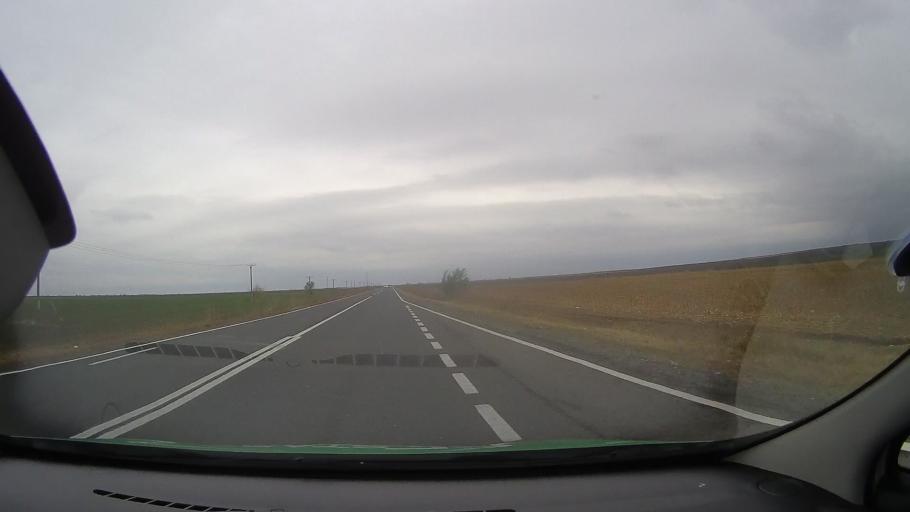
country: RO
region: Constanta
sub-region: Comuna Nicolae Balcescu
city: Nicolae Balcescu
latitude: 44.3800
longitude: 28.4091
